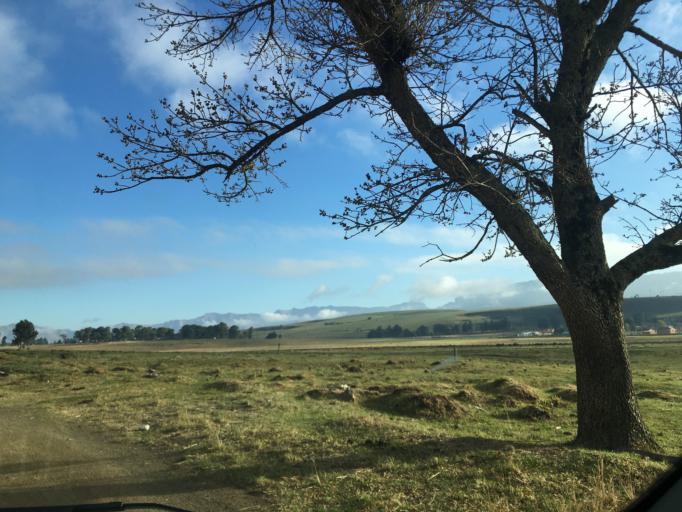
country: ZA
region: Eastern Cape
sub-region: Chris Hani District Municipality
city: Elliot
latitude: -31.3359
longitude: 27.8416
